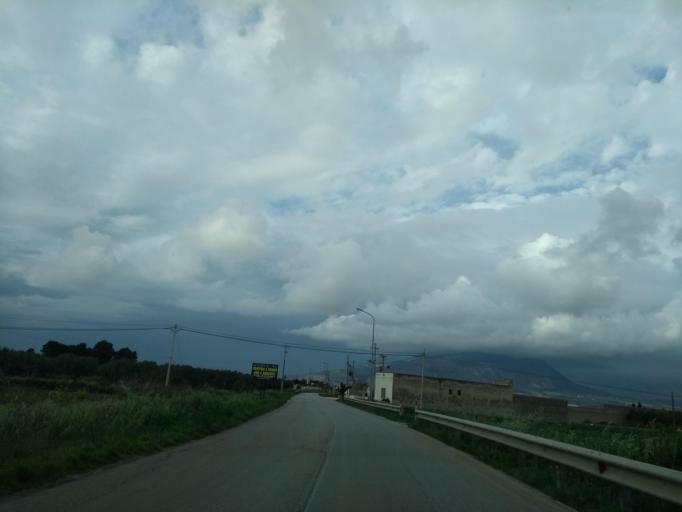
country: IT
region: Sicily
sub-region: Trapani
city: Paceco
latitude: 37.9775
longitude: 12.5285
